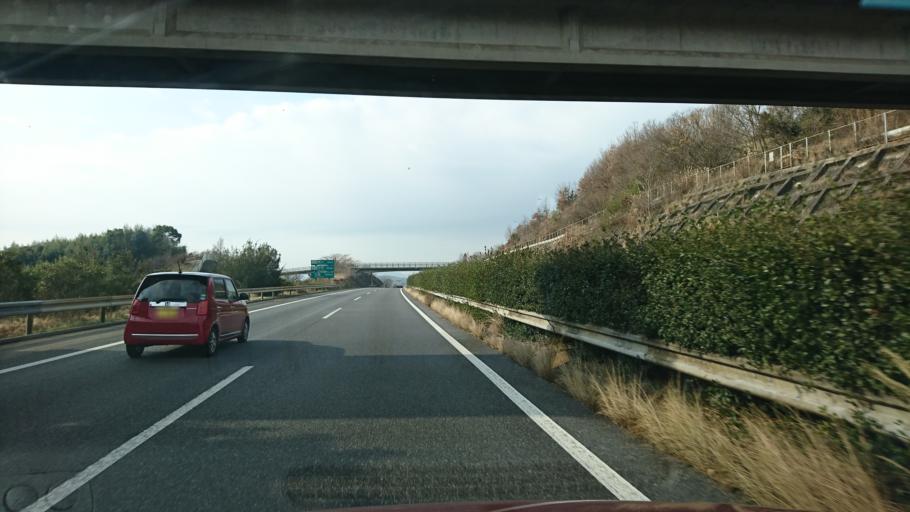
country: JP
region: Okayama
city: Kamogatacho-kamogata
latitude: 34.5729
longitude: 133.6692
